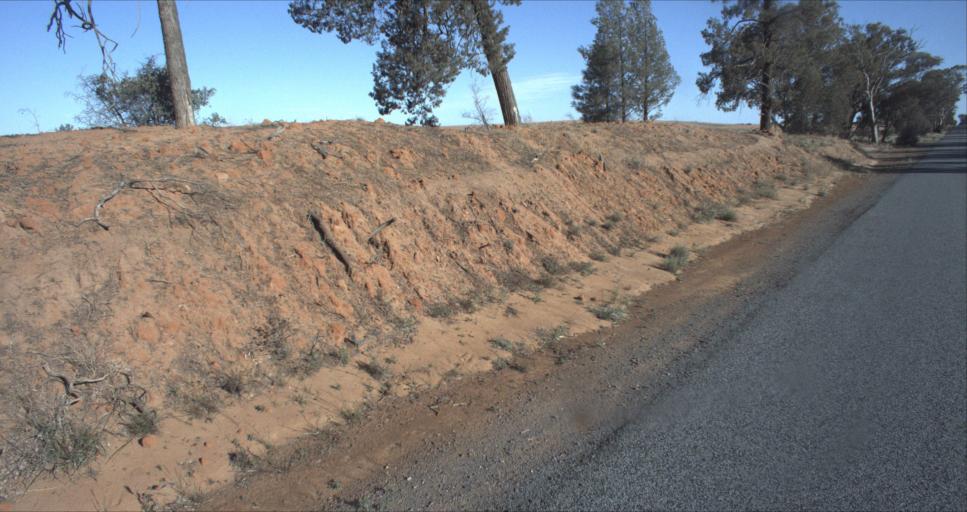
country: AU
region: New South Wales
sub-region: Leeton
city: Leeton
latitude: -34.6520
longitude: 146.3510
